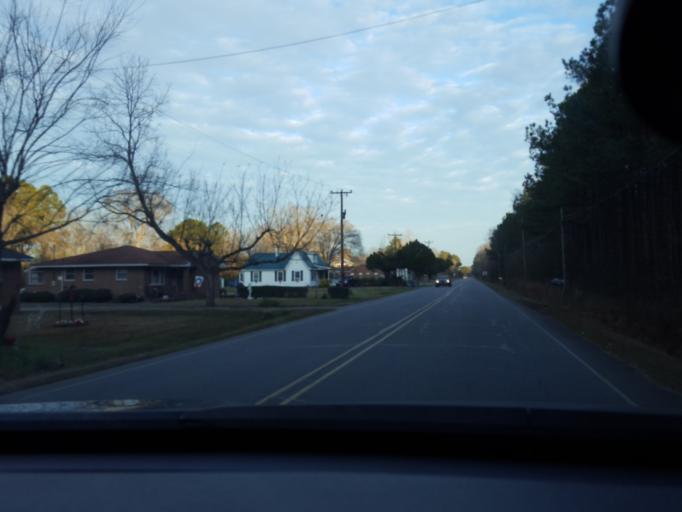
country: US
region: North Carolina
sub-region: Northampton County
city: Jackson
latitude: 36.2694
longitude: -77.2645
